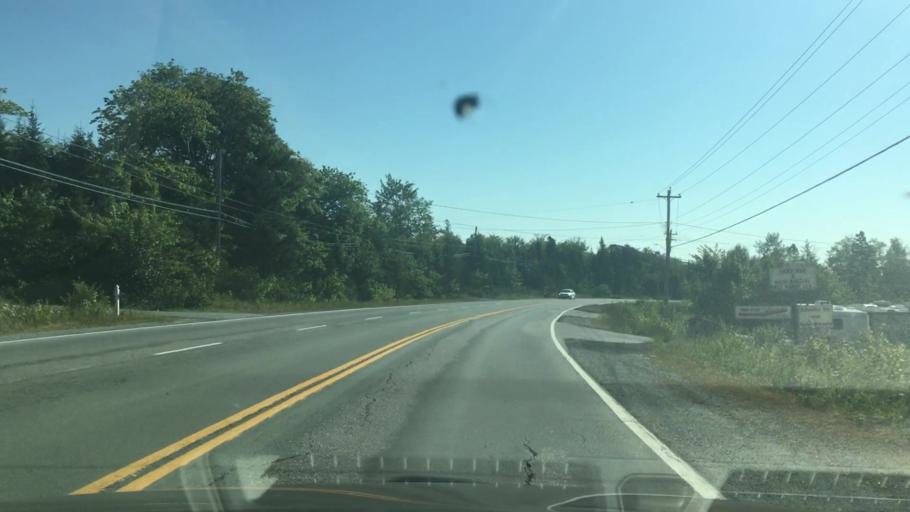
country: CA
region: Nova Scotia
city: Cole Harbour
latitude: 44.7791
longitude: -63.0800
